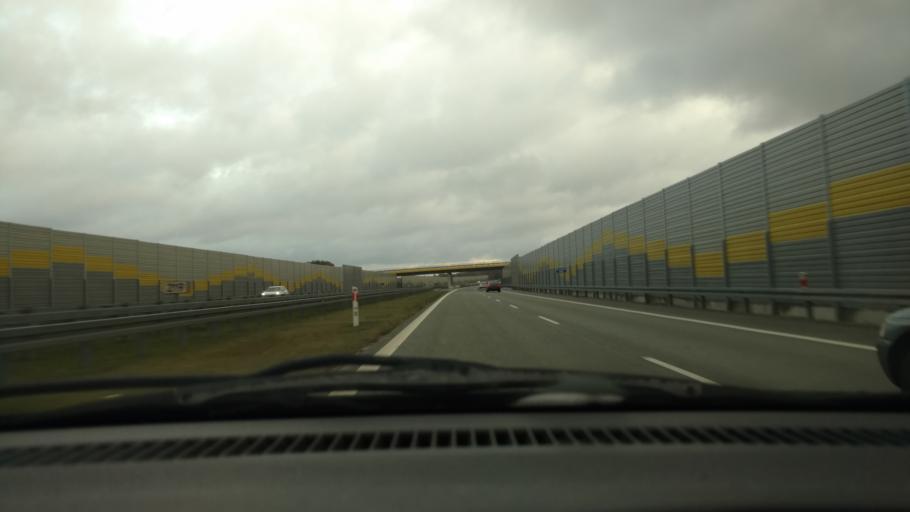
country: PL
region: Lodz Voivodeship
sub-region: Powiat pabianicki
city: Pabianice
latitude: 51.6202
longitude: 19.3811
